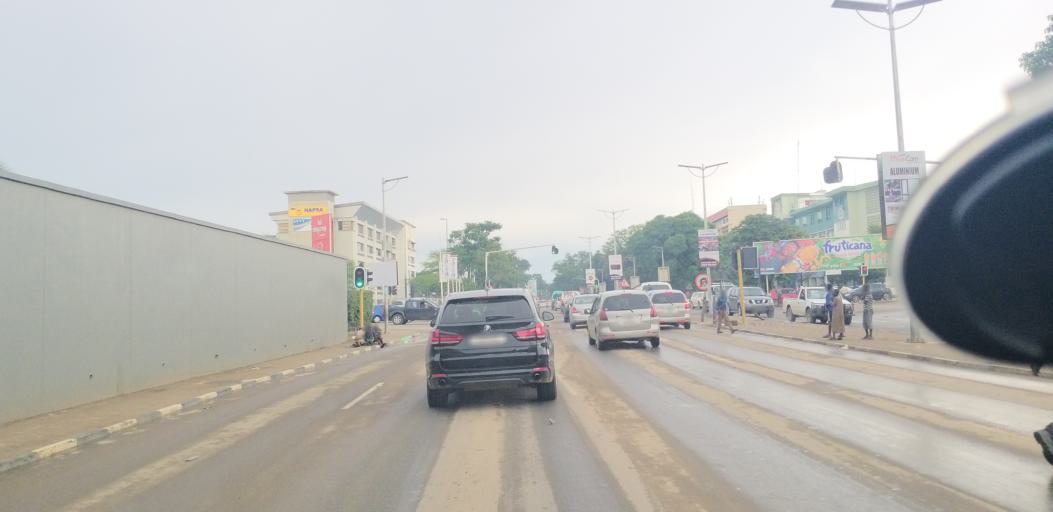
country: ZM
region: Lusaka
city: Lusaka
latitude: -15.4155
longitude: 28.2852
